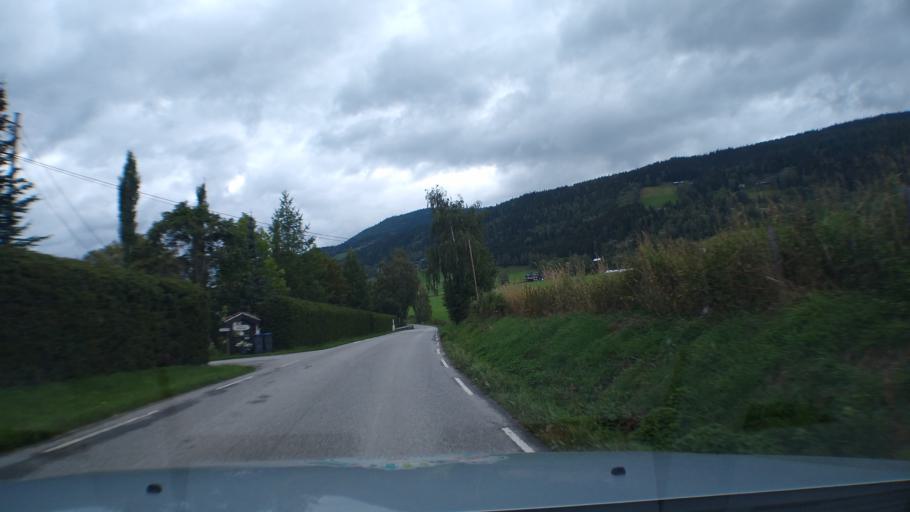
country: NO
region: Oppland
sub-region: Ringebu
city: Ringebu
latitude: 61.5430
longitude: 10.1171
